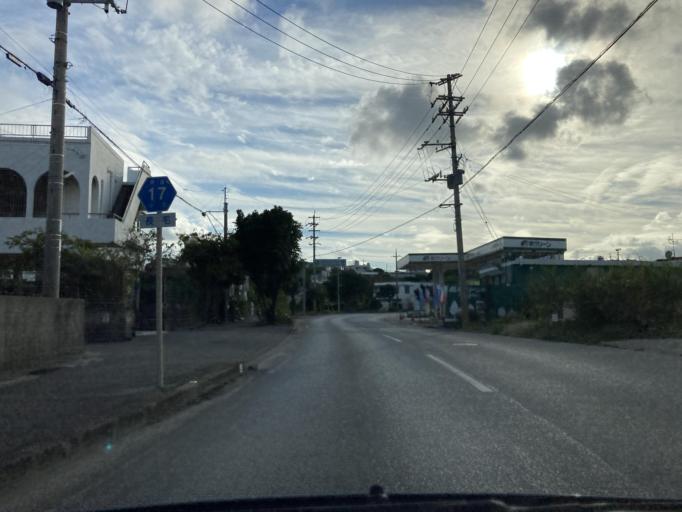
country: JP
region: Okinawa
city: Itoman
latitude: 26.1318
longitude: 127.7586
